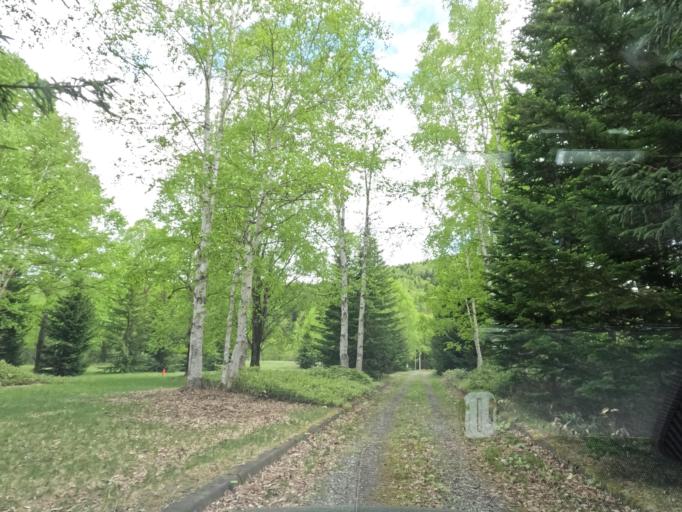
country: JP
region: Hokkaido
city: Kamikawa
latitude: 43.6438
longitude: 143.0224
